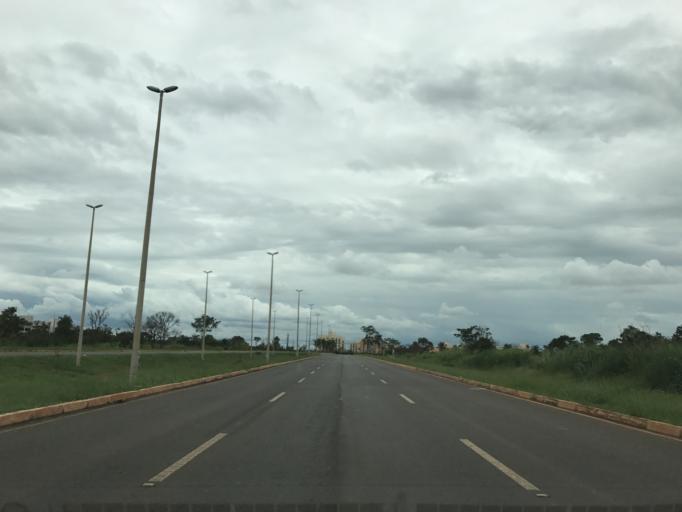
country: BR
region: Federal District
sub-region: Brasilia
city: Brasilia
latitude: -15.8066
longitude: -47.9923
